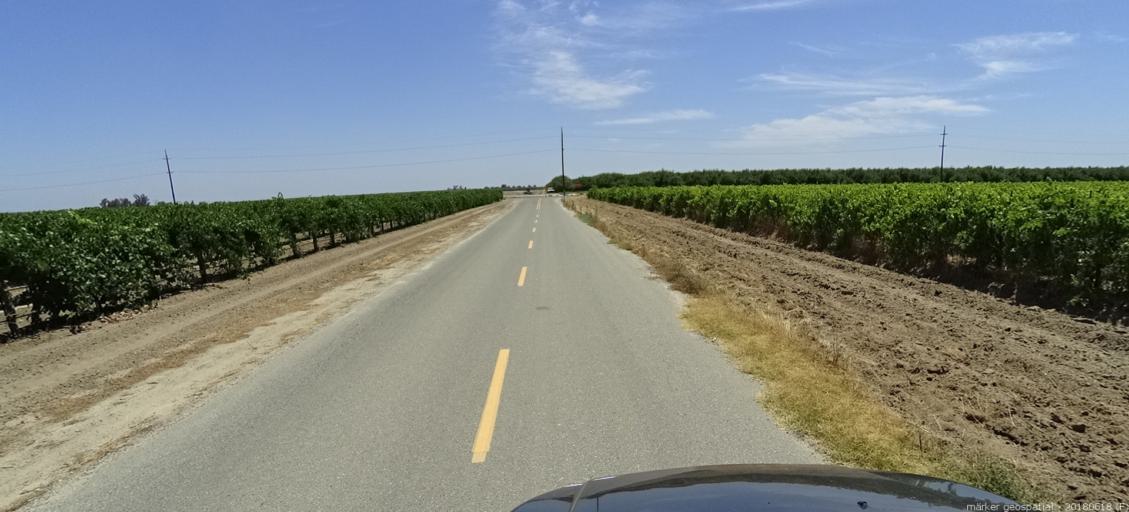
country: US
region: California
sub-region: Madera County
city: Parkwood
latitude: 36.9021
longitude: -120.1120
